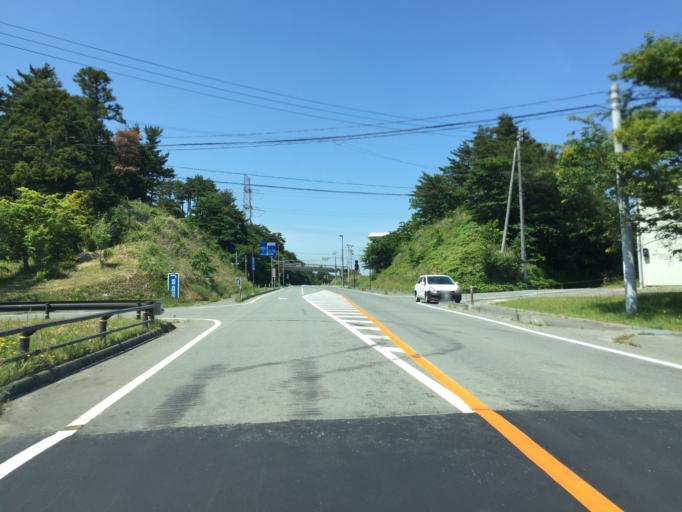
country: JP
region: Fukushima
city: Iwaki
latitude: 37.2361
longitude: 141.0043
